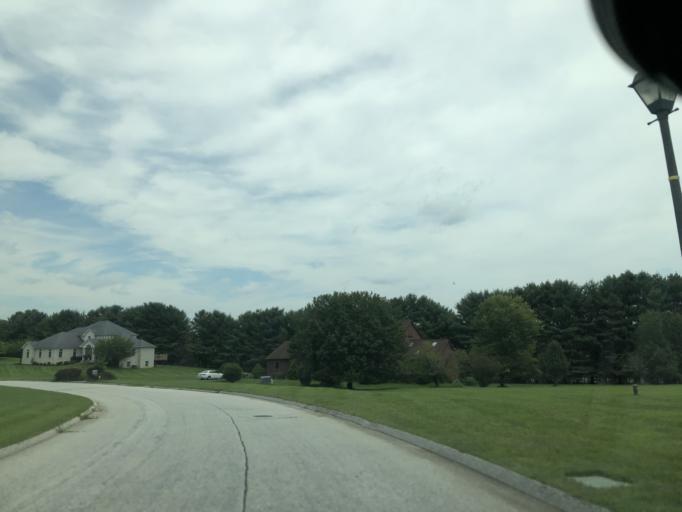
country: US
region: Maryland
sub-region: Baltimore County
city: Garrison
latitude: 39.4483
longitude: -76.7152
